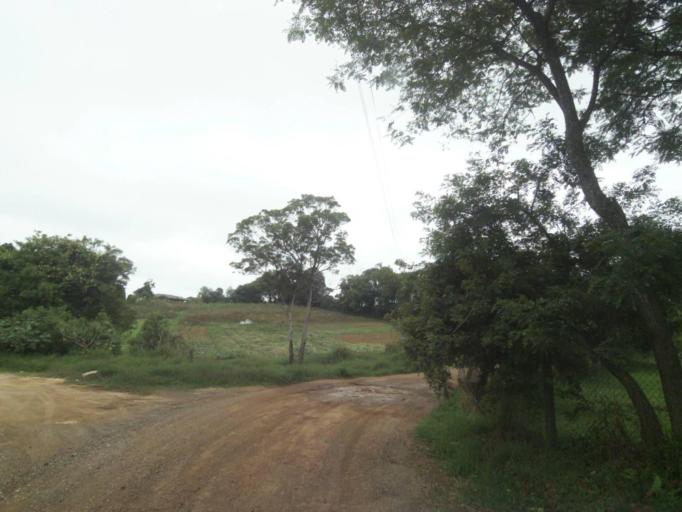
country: BR
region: Parana
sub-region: Curitiba
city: Curitiba
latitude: -25.4965
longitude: -49.3523
